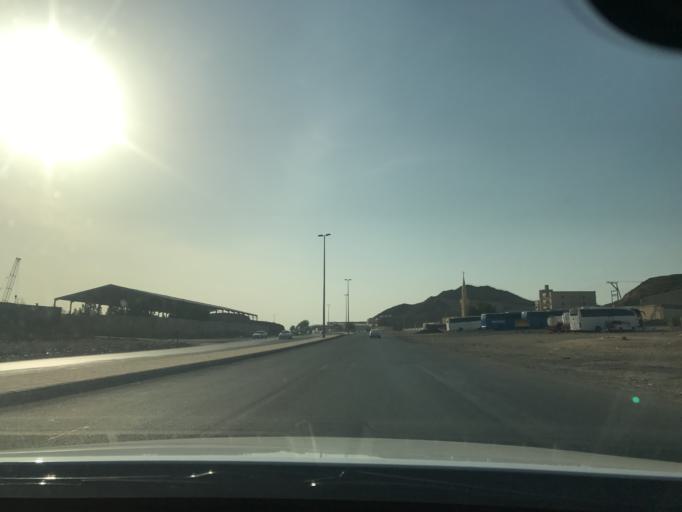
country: SA
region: Makkah
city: Jeddah
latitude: 21.4098
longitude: 39.4246
